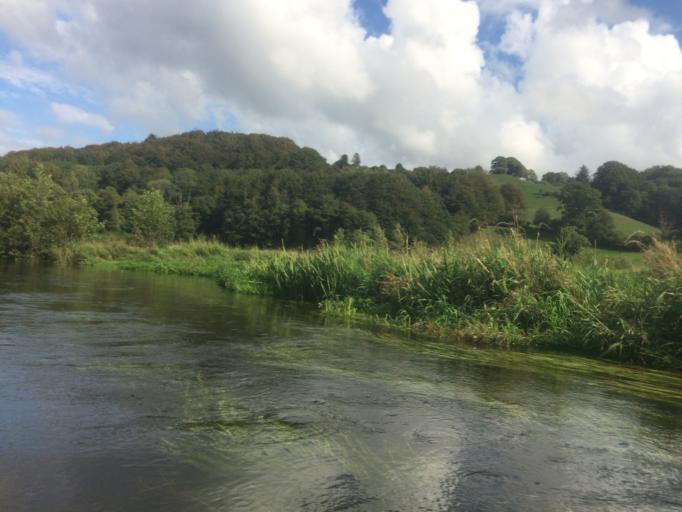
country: DK
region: South Denmark
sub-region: Vejle Kommune
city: Egtved
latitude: 55.6561
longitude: 9.3126
